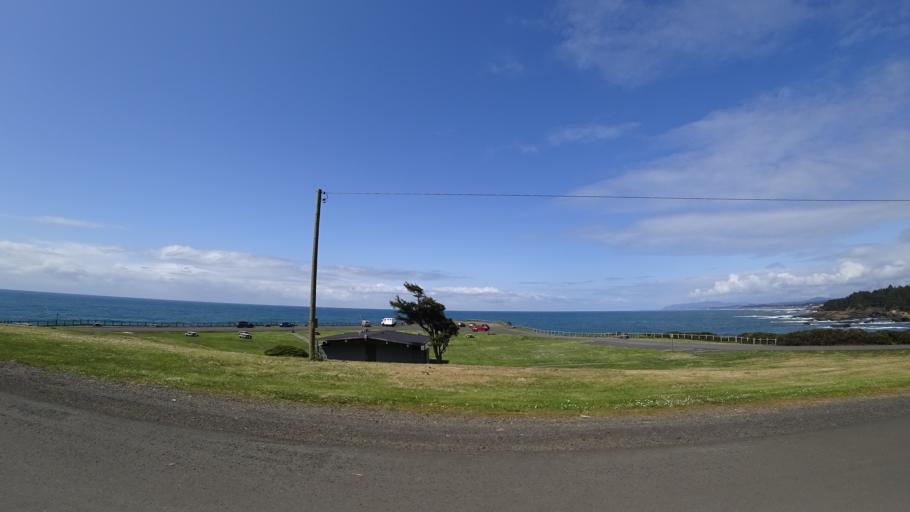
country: US
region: Oregon
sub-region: Lincoln County
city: Depoe Bay
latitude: 44.8284
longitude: -124.0641
